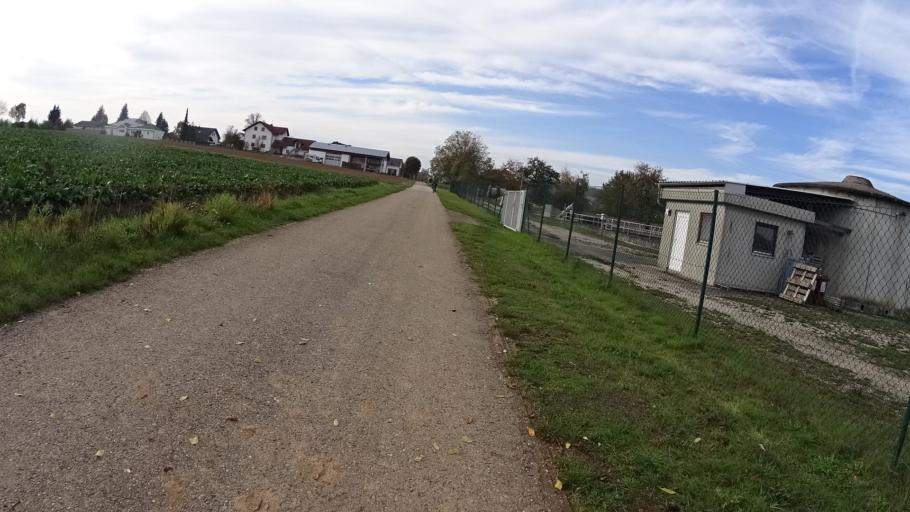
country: DE
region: Bavaria
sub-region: Upper Bavaria
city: Adelschlag
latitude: 48.8571
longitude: 11.2463
